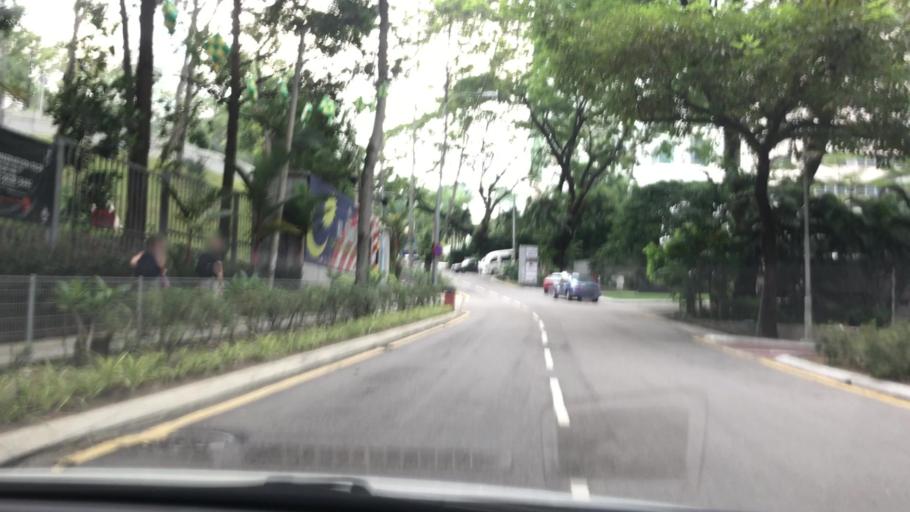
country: MY
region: Kuala Lumpur
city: Kuala Lumpur
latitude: 3.1518
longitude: 101.7062
